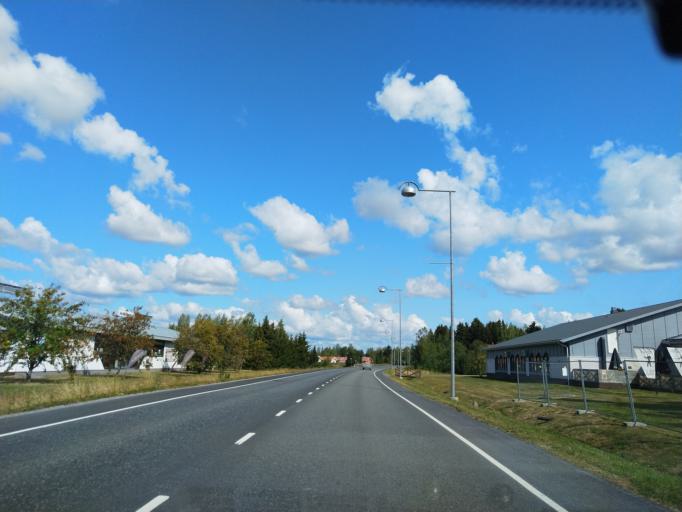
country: FI
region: Satakunta
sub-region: Pori
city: Huittinen
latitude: 61.1699
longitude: 22.7082
